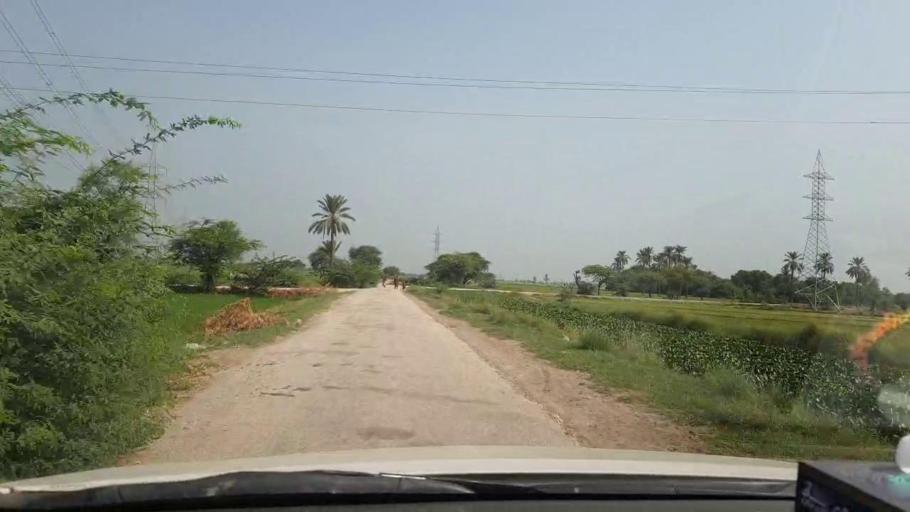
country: PK
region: Sindh
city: Shikarpur
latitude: 27.9794
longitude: 68.6640
